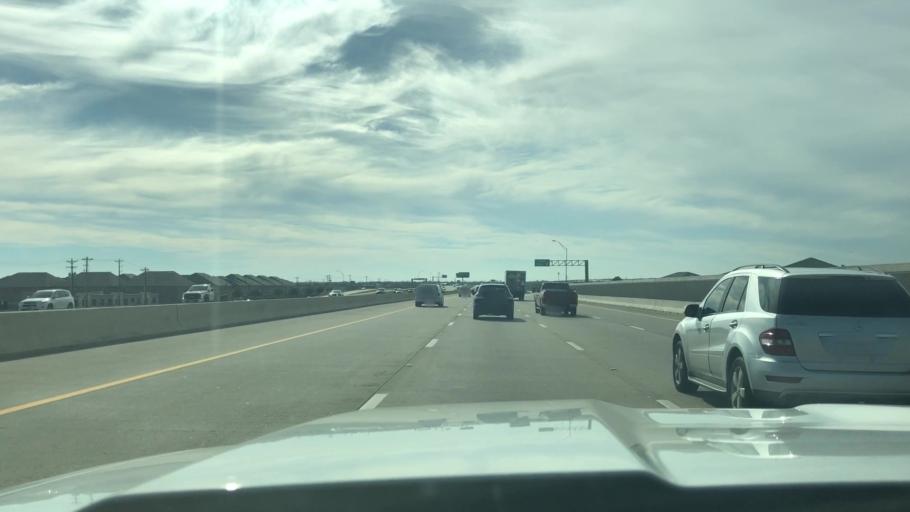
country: US
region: Texas
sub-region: Denton County
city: Lewisville
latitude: 33.0297
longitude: -96.9291
